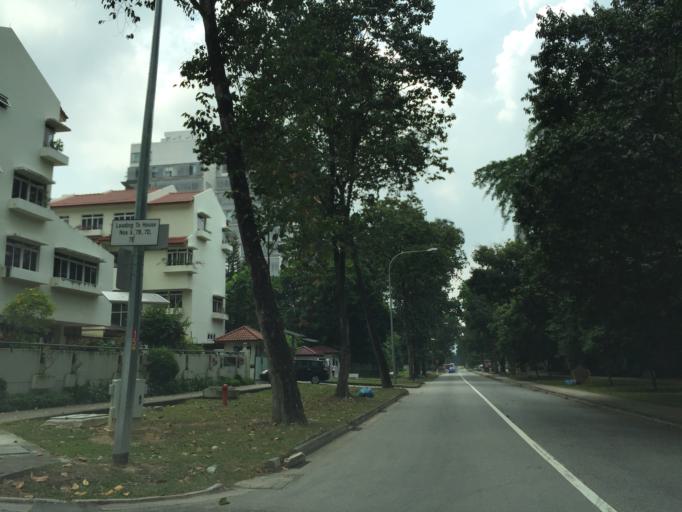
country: SG
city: Singapore
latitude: 1.3138
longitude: 103.8309
